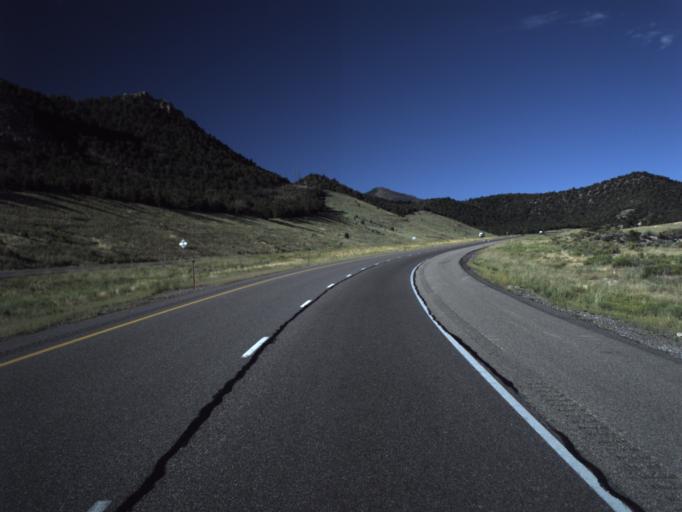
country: US
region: Utah
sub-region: Sevier County
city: Monroe
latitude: 38.5539
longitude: -112.3644
